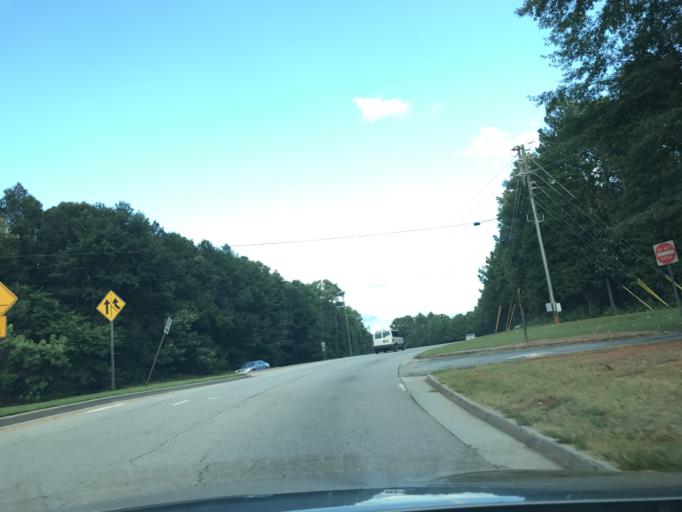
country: US
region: Georgia
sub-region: Douglas County
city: Douglasville
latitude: 33.7360
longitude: -84.7370
